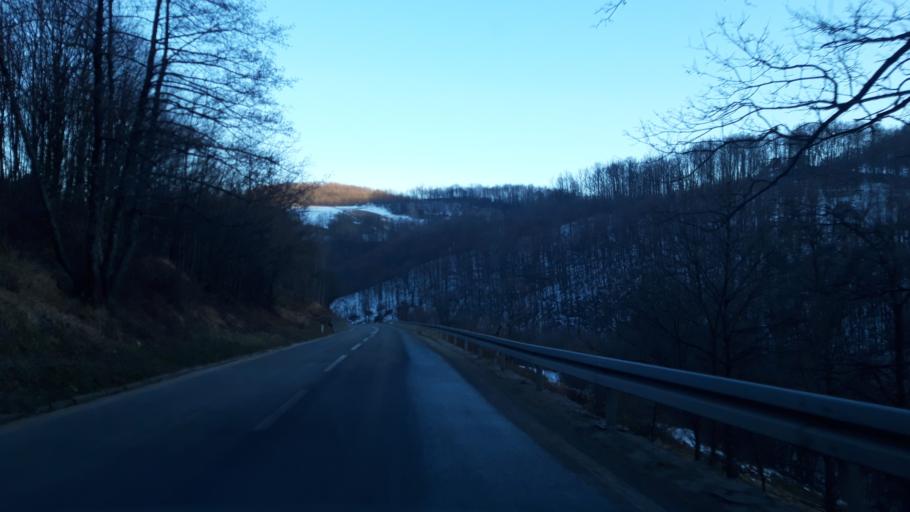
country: BA
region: Republika Srpska
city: Vlasenica
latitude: 44.1809
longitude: 18.9779
